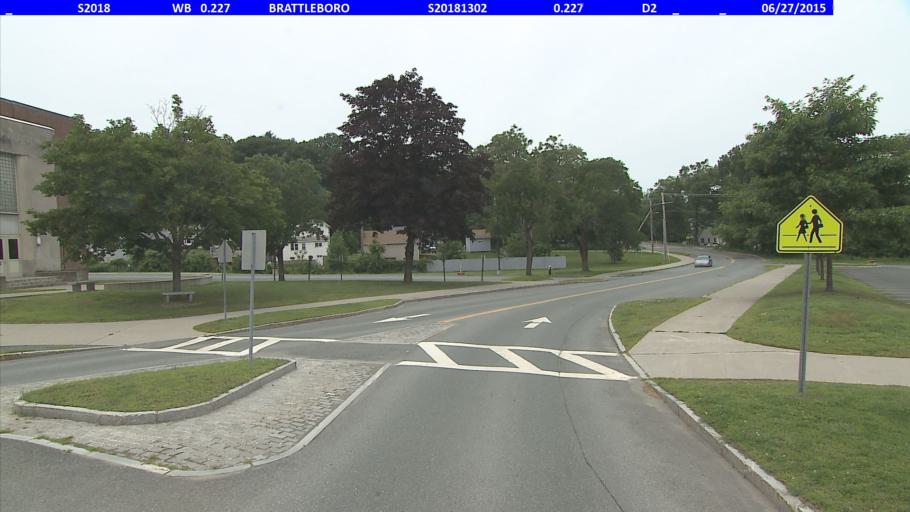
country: US
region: Vermont
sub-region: Windham County
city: Brattleboro
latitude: 42.8373
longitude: -72.5612
